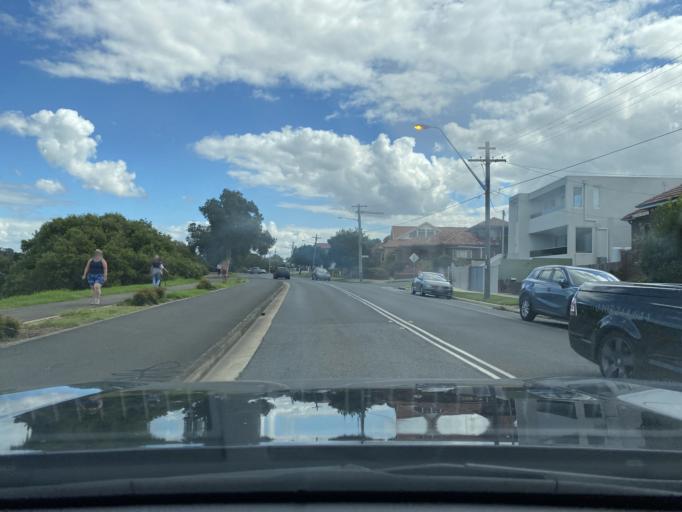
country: AU
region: New South Wales
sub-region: Leichhardt
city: Leichhardt
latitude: -33.8667
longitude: 151.1460
